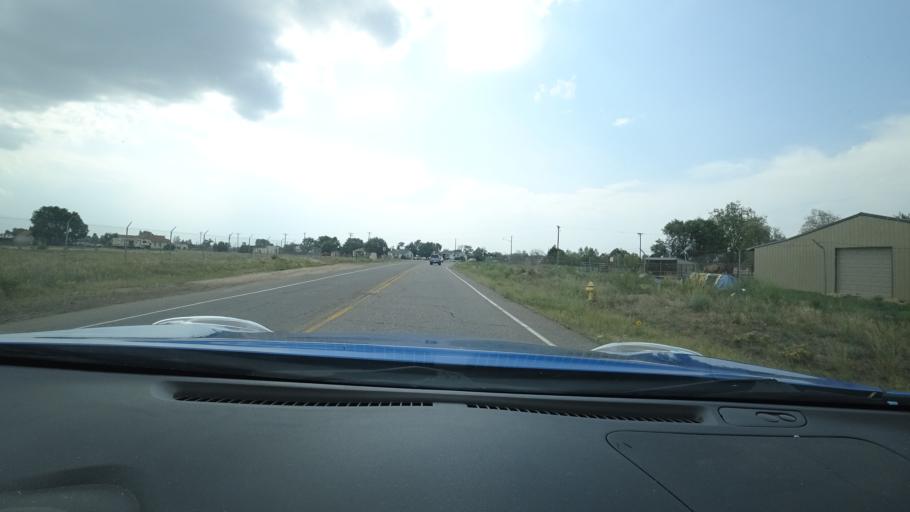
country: US
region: Colorado
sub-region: Adams County
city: Todd Creek
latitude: 39.9216
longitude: -104.8631
